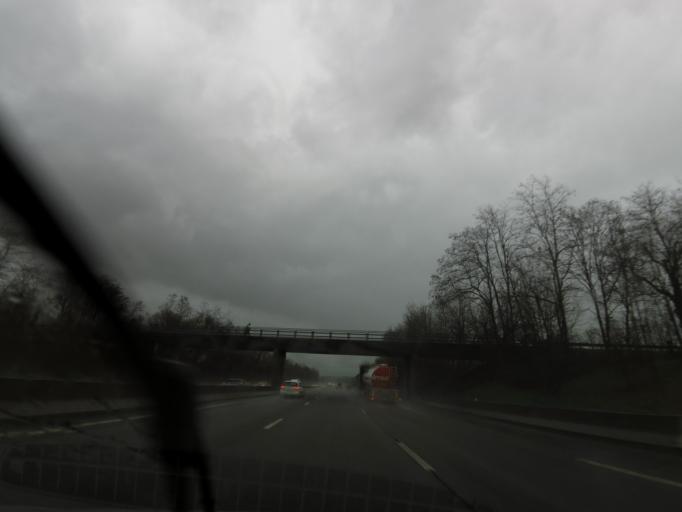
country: FR
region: Rhone-Alpes
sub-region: Departement de l'Ain
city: Montagnat
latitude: 46.1628
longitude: 5.2981
